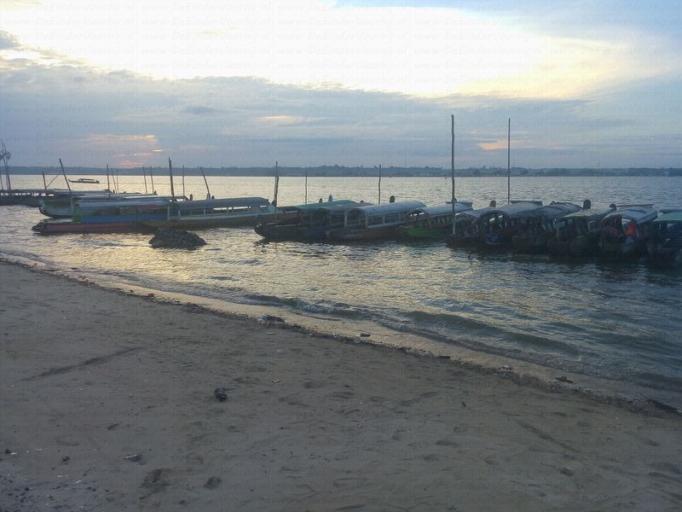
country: GF
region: Guyane
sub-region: Guyane
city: Saint-Laurent-du-Maroni
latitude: 5.4905
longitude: -54.0379
